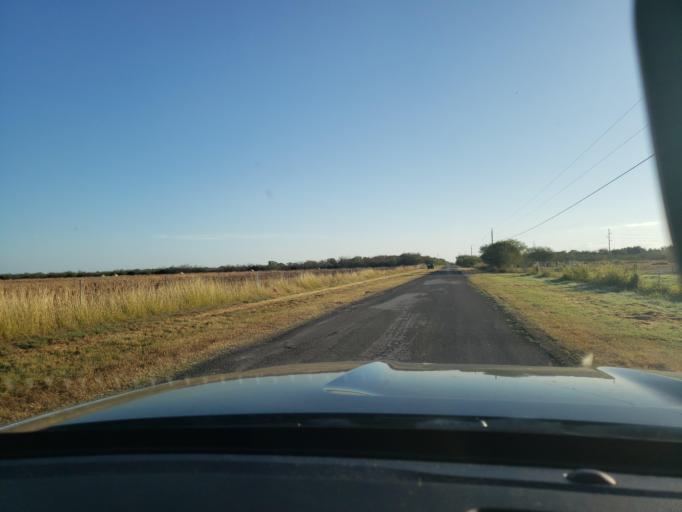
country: US
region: Texas
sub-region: Bee County
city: Beeville
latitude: 28.4311
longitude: -97.6891
